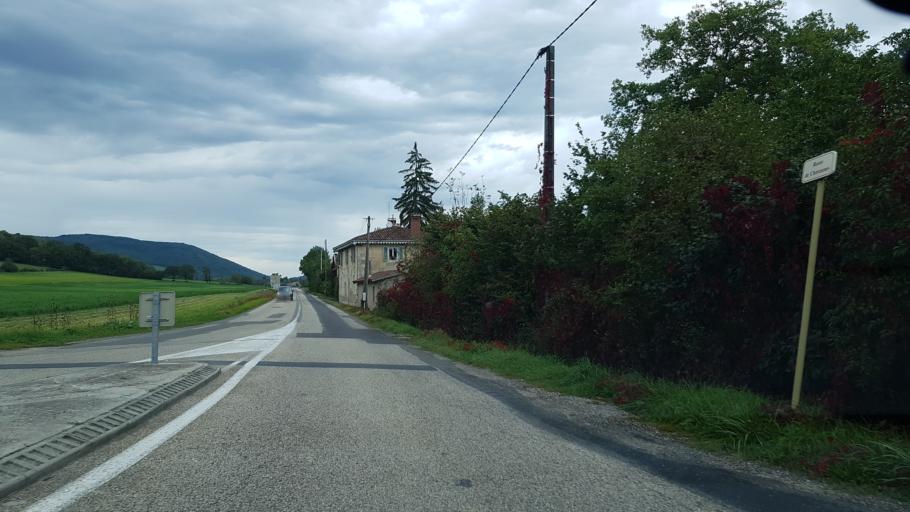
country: FR
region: Rhone-Alpes
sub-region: Departement de l'Ain
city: Cuisiat
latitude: 46.2467
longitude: 5.4232
